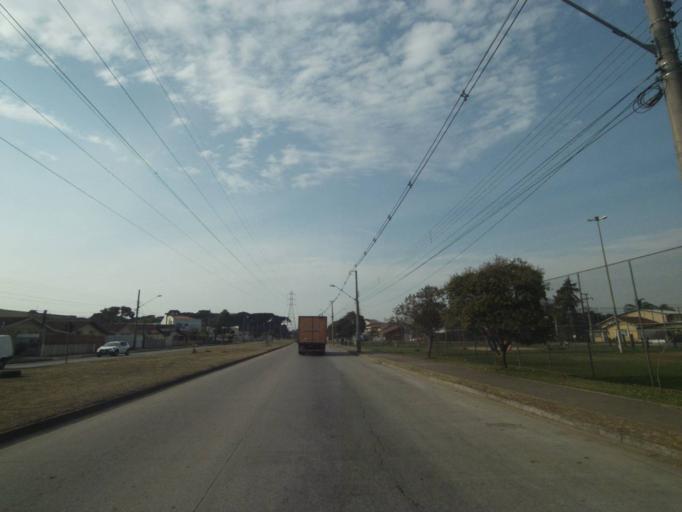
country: BR
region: Parana
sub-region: Sao Jose Dos Pinhais
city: Sao Jose dos Pinhais
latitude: -25.4943
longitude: -49.2082
